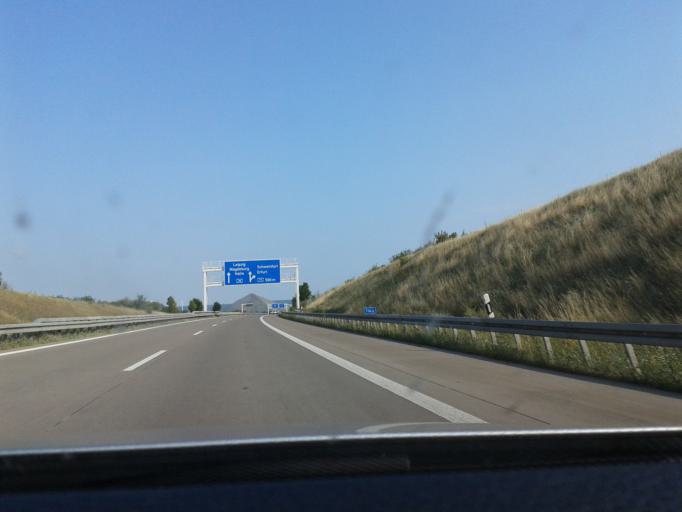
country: DE
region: Saxony-Anhalt
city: Oberroblingen
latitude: 51.4480
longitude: 11.3180
